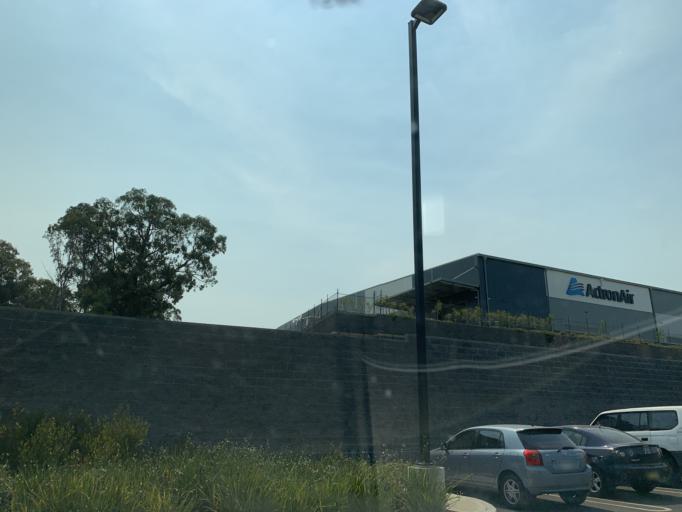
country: AU
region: New South Wales
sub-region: Blacktown
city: Hassall Grove
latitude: -33.7222
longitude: 150.8398
